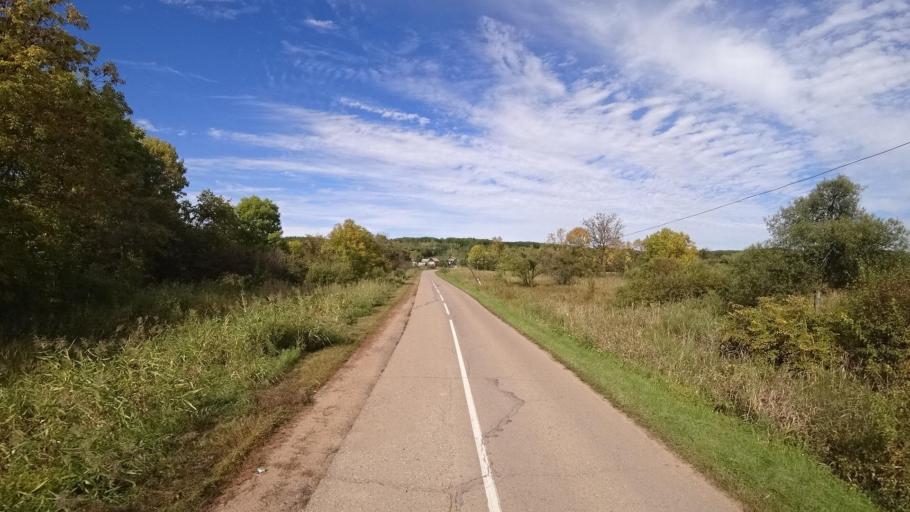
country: RU
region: Primorskiy
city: Dostoyevka
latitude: 44.3315
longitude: 133.4812
